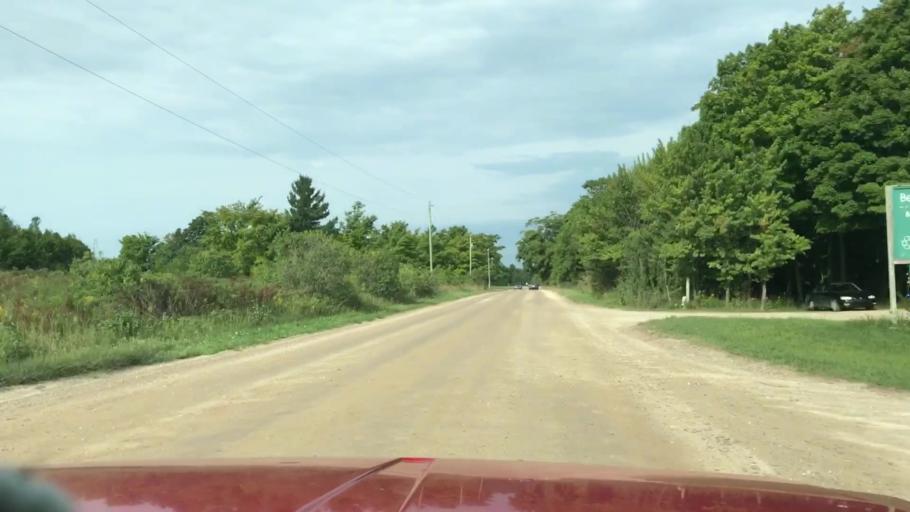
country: US
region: Michigan
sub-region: Charlevoix County
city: Charlevoix
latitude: 45.7285
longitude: -85.5199
